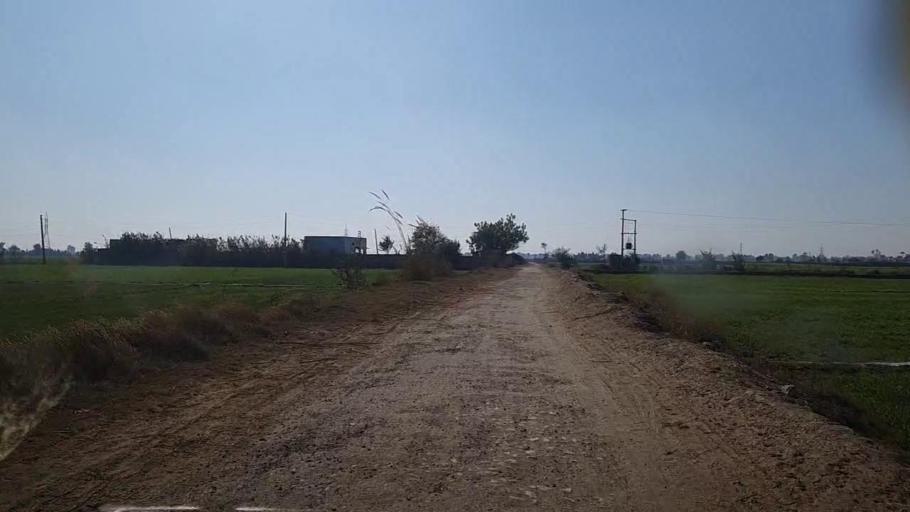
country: PK
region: Sindh
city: Khairpur
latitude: 28.0456
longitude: 69.7831
